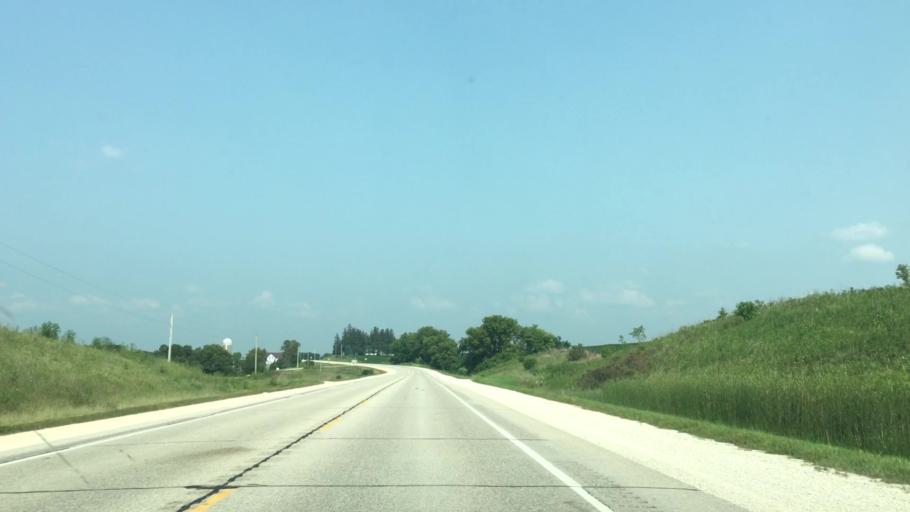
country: US
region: Iowa
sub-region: Winneshiek County
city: Decorah
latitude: 43.2762
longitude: -91.8179
